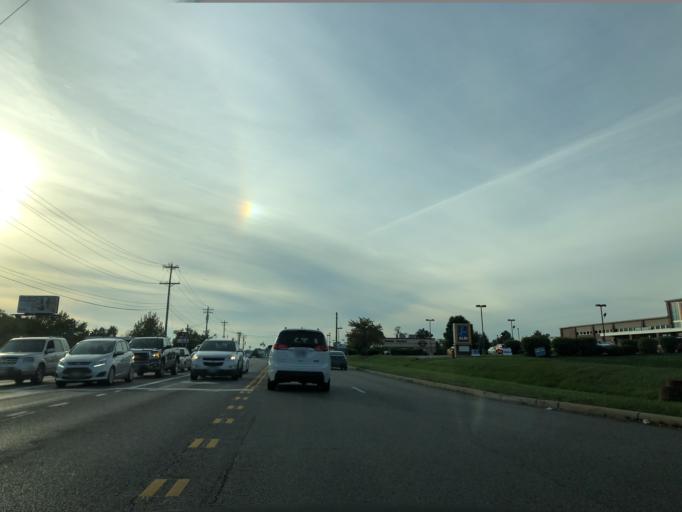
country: US
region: Ohio
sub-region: Warren County
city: Landen
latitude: 39.2907
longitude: -84.2989
